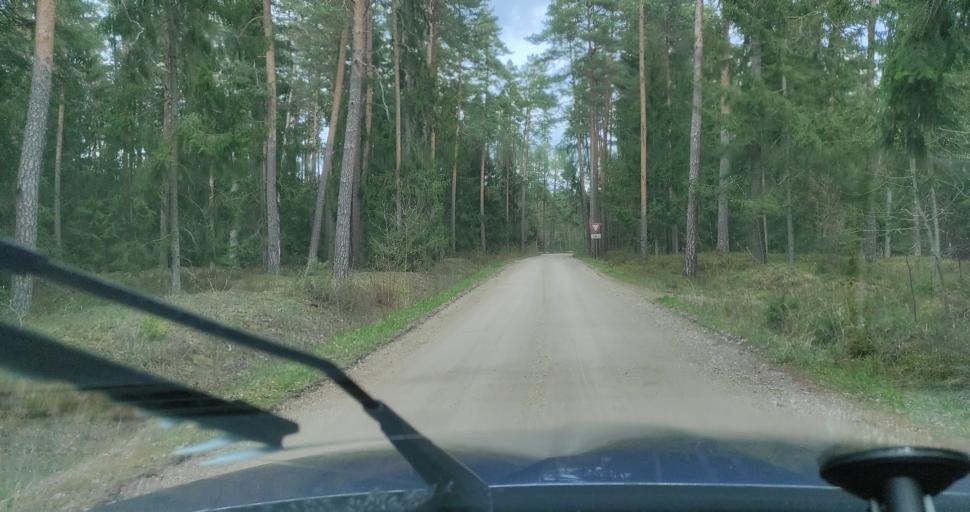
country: LV
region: Talsu Rajons
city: Stende
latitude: 57.2190
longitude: 22.2488
